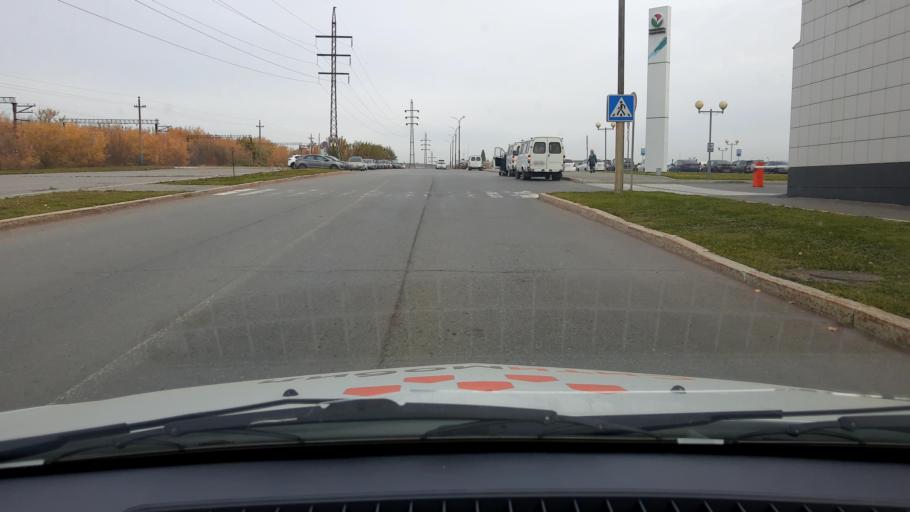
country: RU
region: Bashkortostan
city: Ufa
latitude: 54.8759
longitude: 56.1010
